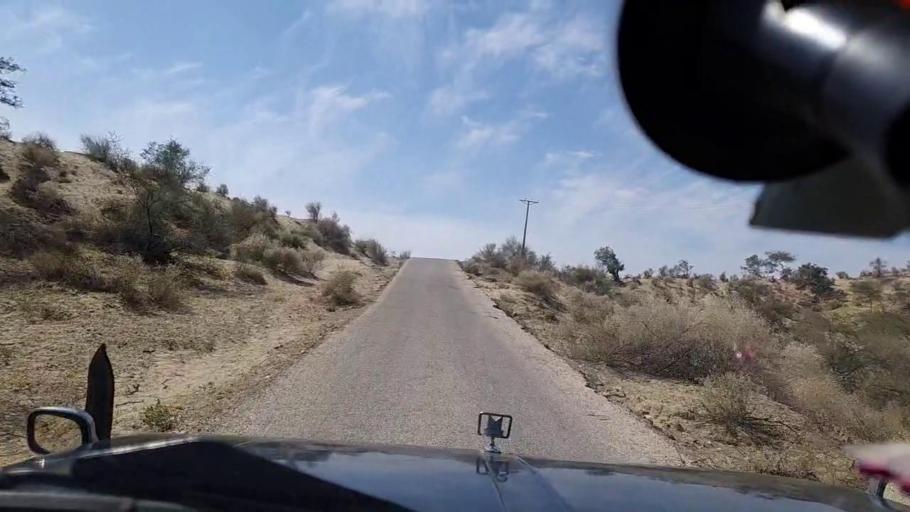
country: PK
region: Sindh
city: Diplo
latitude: 24.3836
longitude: 69.5864
